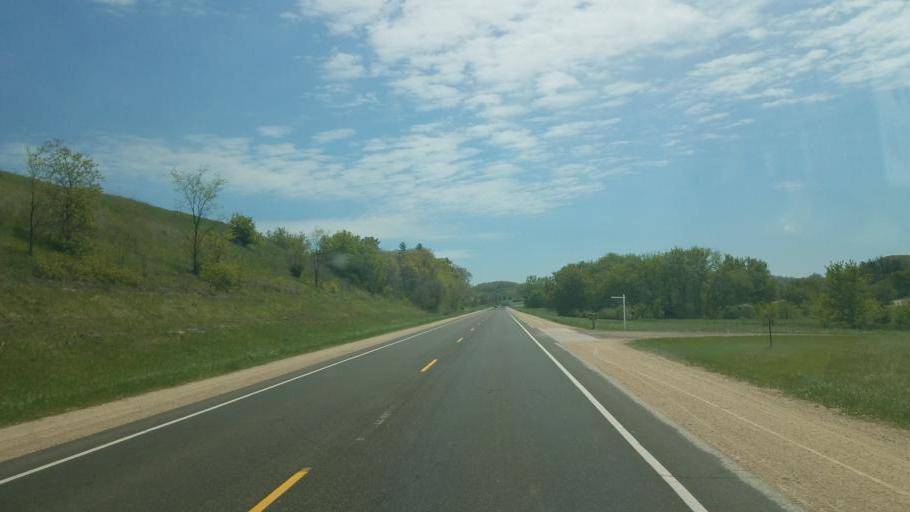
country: US
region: Wisconsin
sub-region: Monroe County
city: Tomah
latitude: 43.9251
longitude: -90.5003
